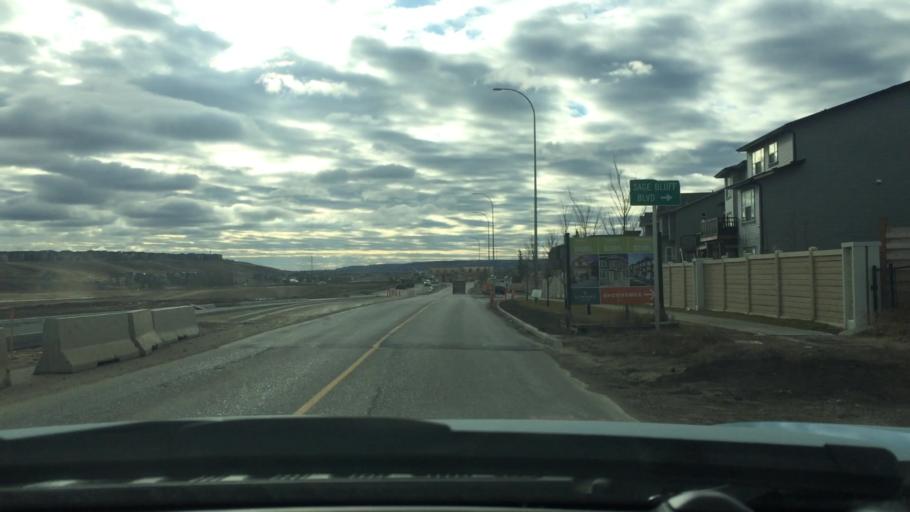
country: CA
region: Alberta
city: Calgary
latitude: 51.1819
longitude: -114.1346
